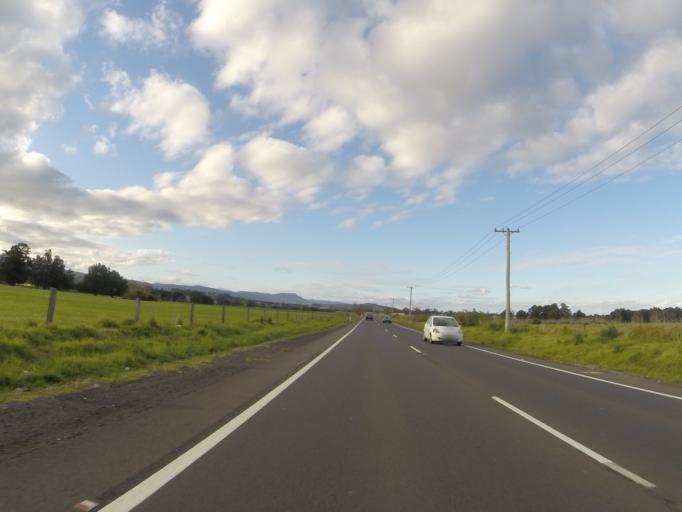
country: AU
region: New South Wales
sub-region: Shellharbour
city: Albion Park Rail
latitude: -34.5628
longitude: 150.7768
